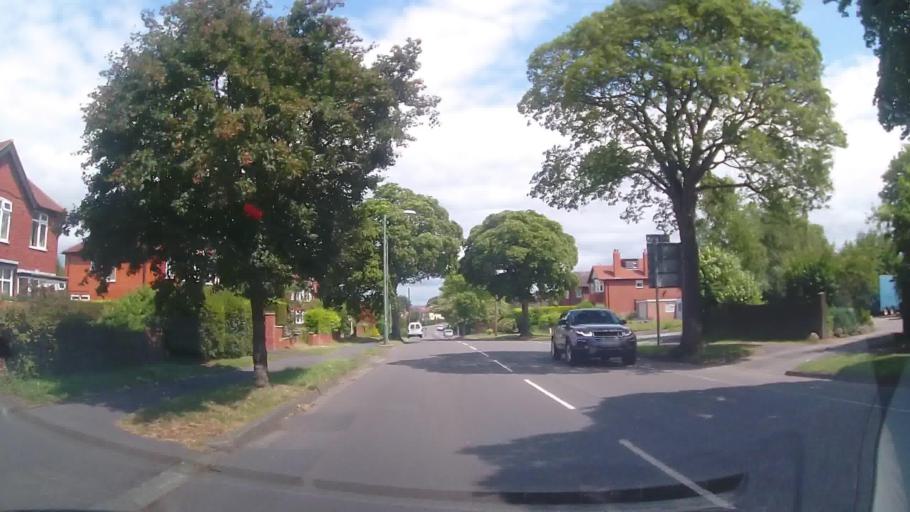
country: GB
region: England
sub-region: Shropshire
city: Shrewsbury
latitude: 52.7085
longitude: -2.7788
